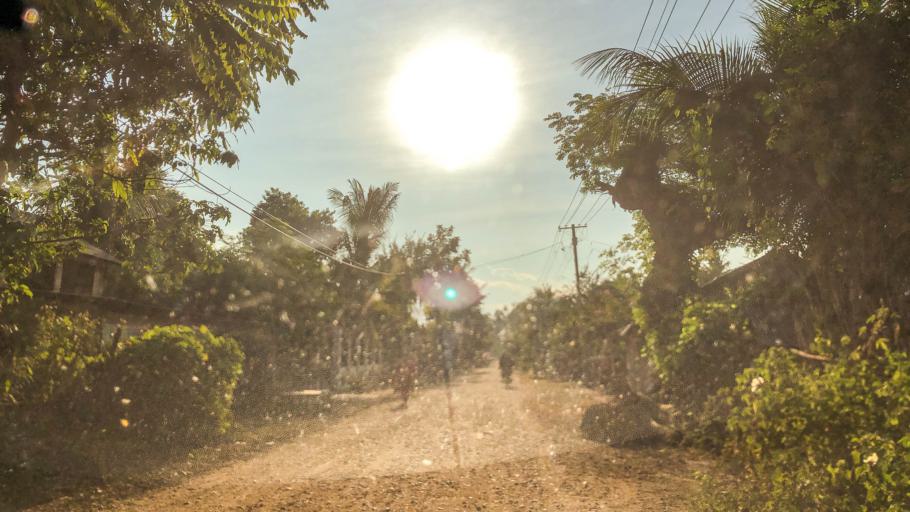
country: MM
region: Magway
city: Magway
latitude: 19.9744
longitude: 95.0373
